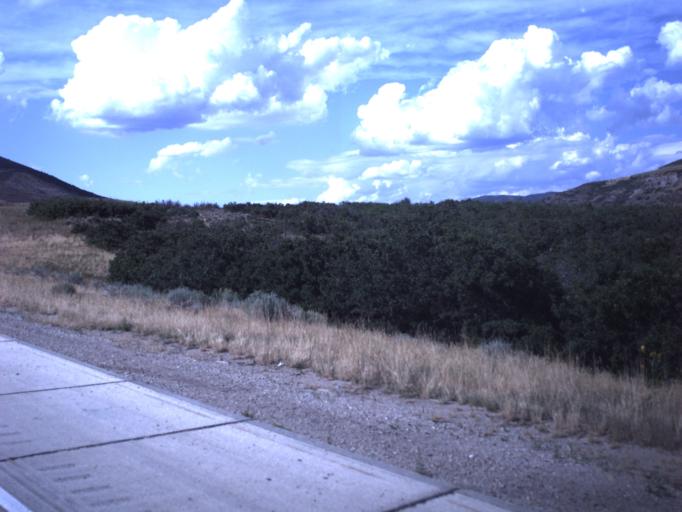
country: US
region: Utah
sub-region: Wasatch County
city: Heber
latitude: 40.5759
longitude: -111.4346
